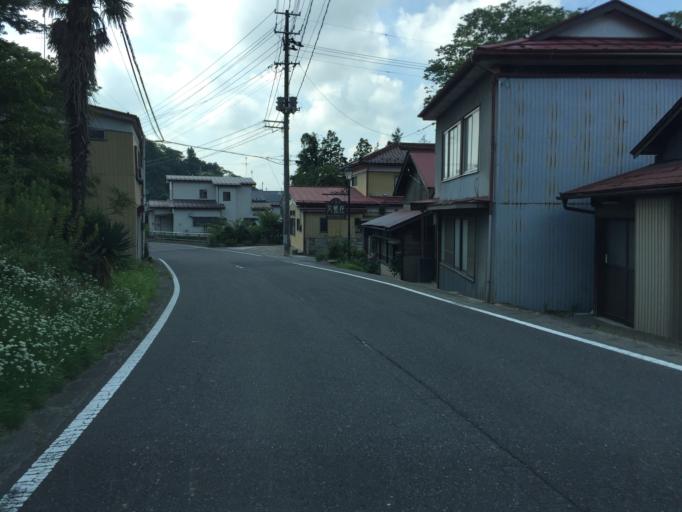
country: JP
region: Fukushima
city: Motomiya
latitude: 37.5245
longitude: 140.4032
